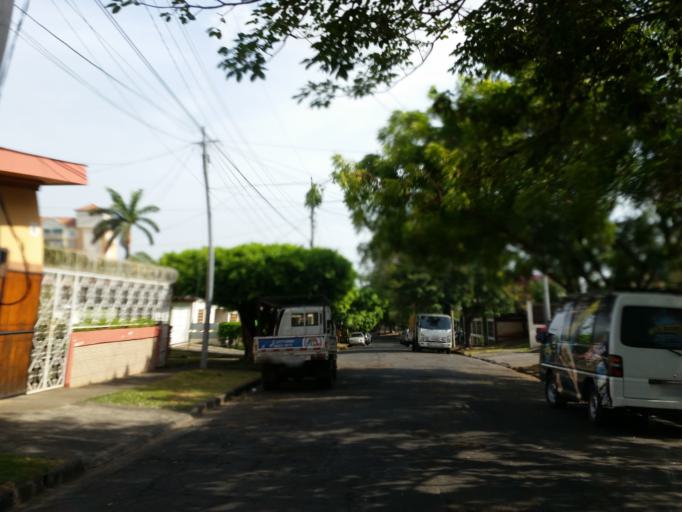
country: NI
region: Managua
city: Managua
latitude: 12.1246
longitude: -86.2635
